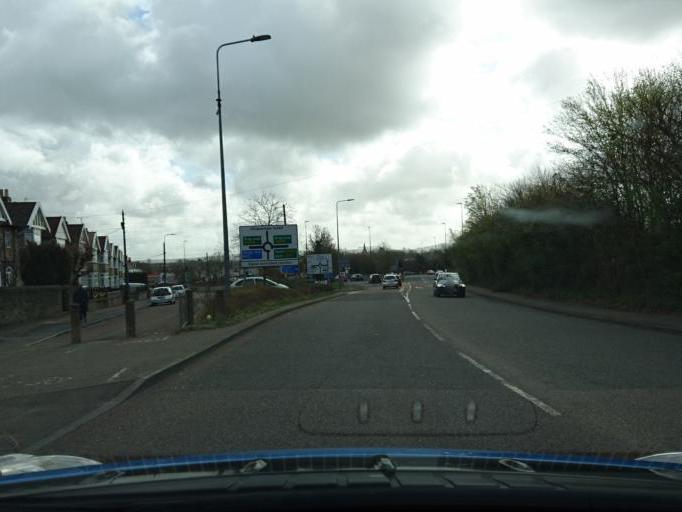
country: GB
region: England
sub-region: South Gloucestershire
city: Kingswood
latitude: 51.4603
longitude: -2.4847
